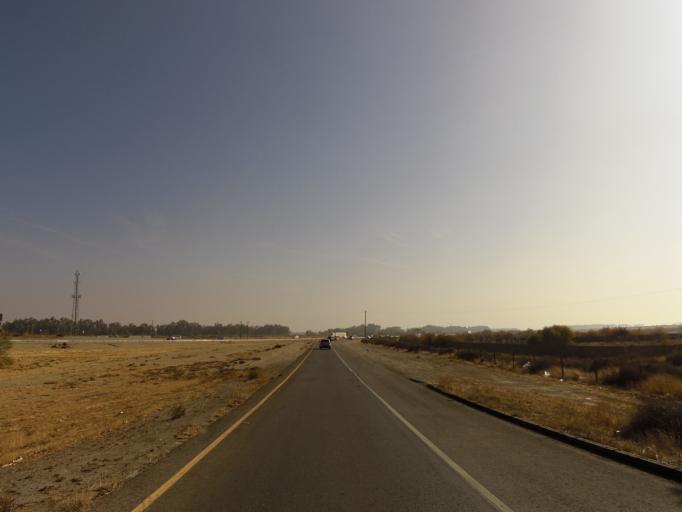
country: US
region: California
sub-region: Kern County
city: Lost Hills
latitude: 35.6155
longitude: -119.6546
